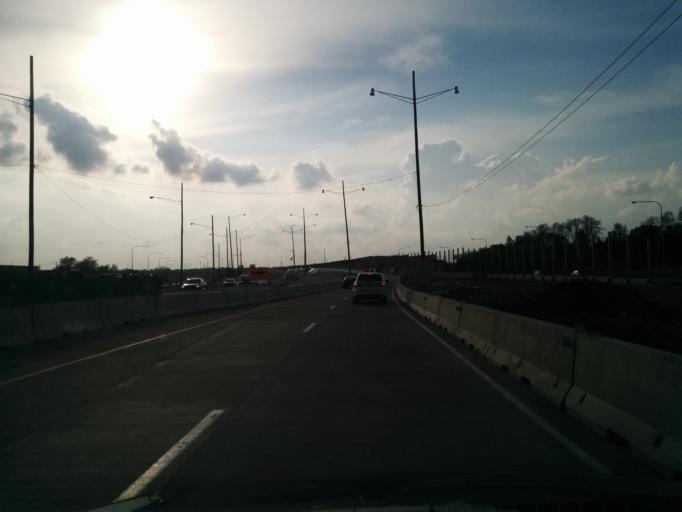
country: US
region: Illinois
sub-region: DuPage County
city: Itasca
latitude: 41.9907
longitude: -88.0415
